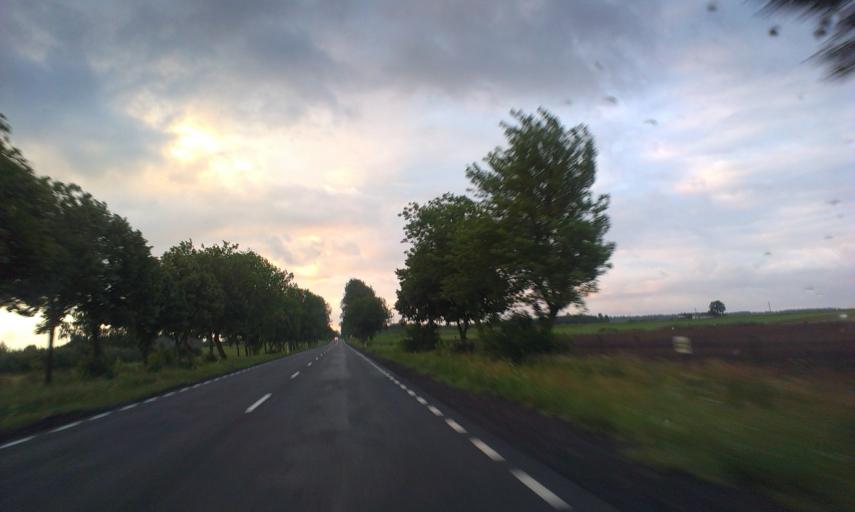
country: PL
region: West Pomeranian Voivodeship
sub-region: Powiat szczecinecki
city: Szczecinek
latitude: 53.6566
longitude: 16.7371
